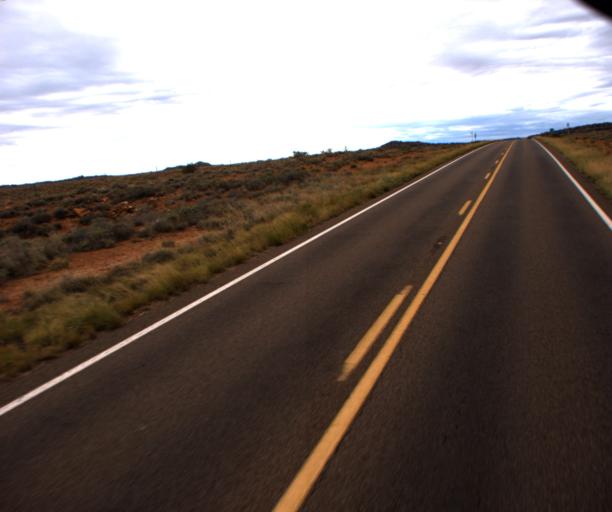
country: US
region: Arizona
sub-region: Navajo County
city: Holbrook
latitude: 34.7132
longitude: -110.1121
